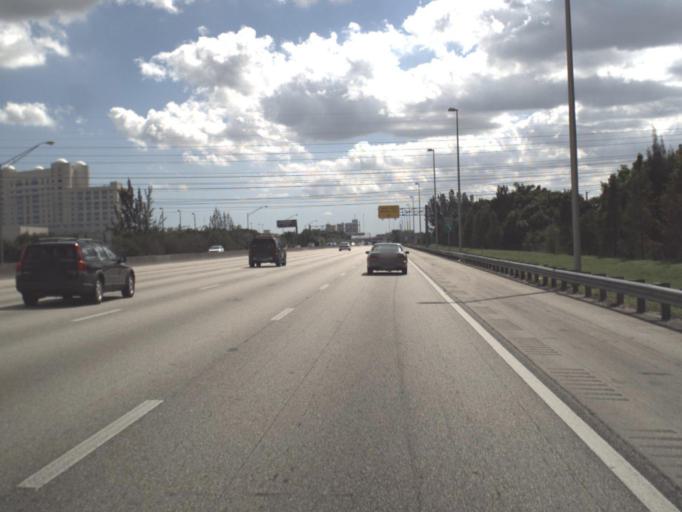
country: US
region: Florida
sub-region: Broward County
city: Davie
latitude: 26.0573
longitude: -80.2153
